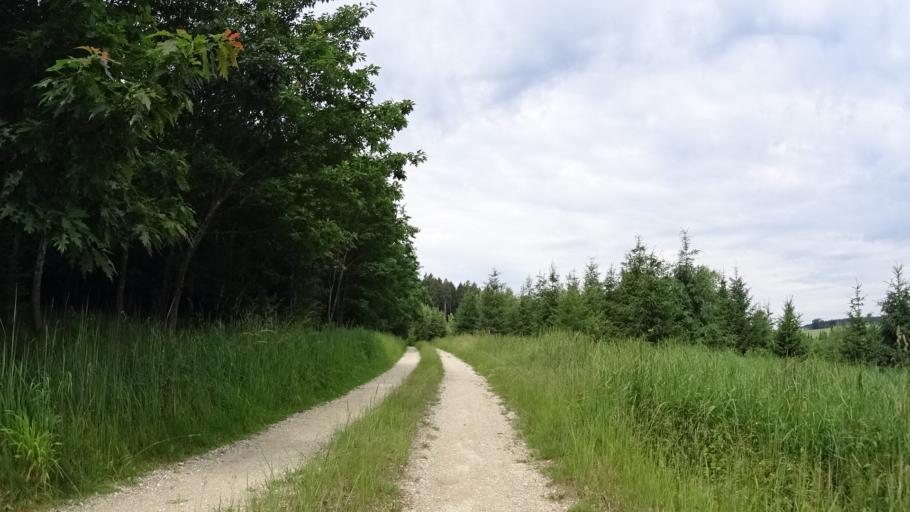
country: DE
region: Bavaria
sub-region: Upper Bavaria
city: Denkendorf
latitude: 48.9104
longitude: 11.4958
